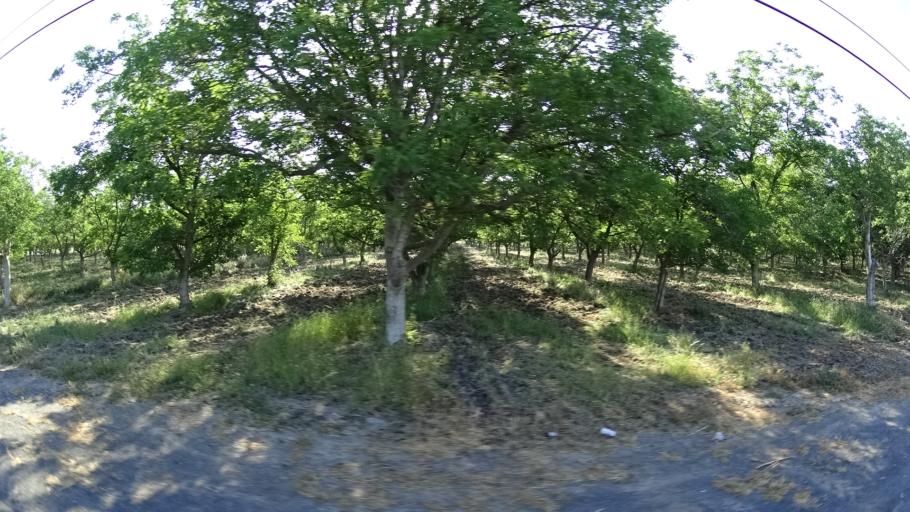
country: US
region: California
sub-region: Kings County
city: Armona
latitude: 36.2825
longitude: -119.7091
